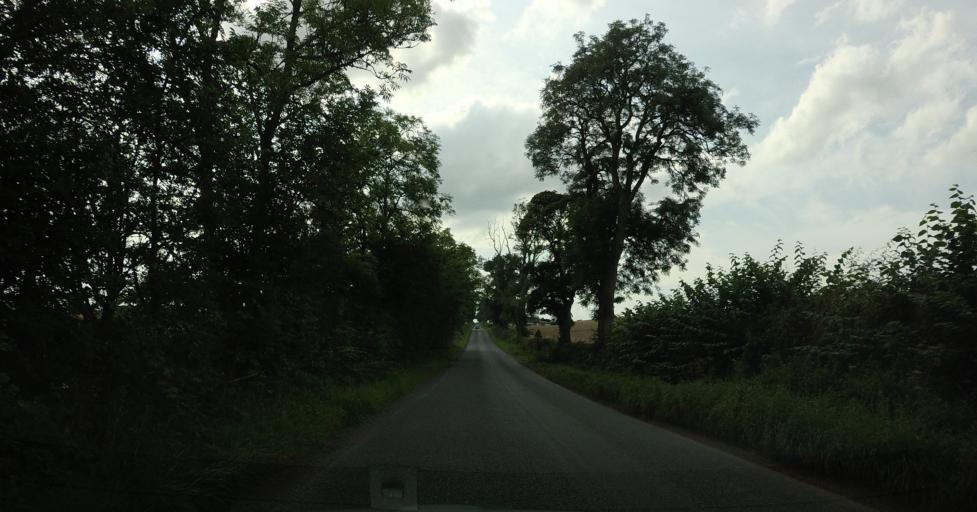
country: GB
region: Scotland
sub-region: Perth and Kinross
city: Methven
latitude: 56.3775
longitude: -3.6613
